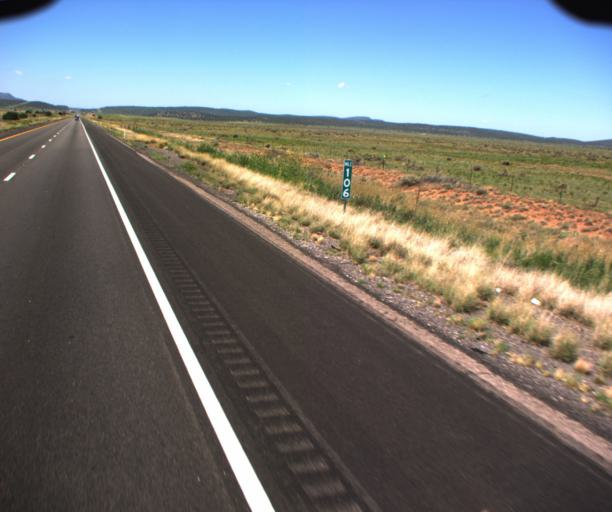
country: US
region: Arizona
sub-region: Mohave County
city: Peach Springs
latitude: 35.2714
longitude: -113.1438
